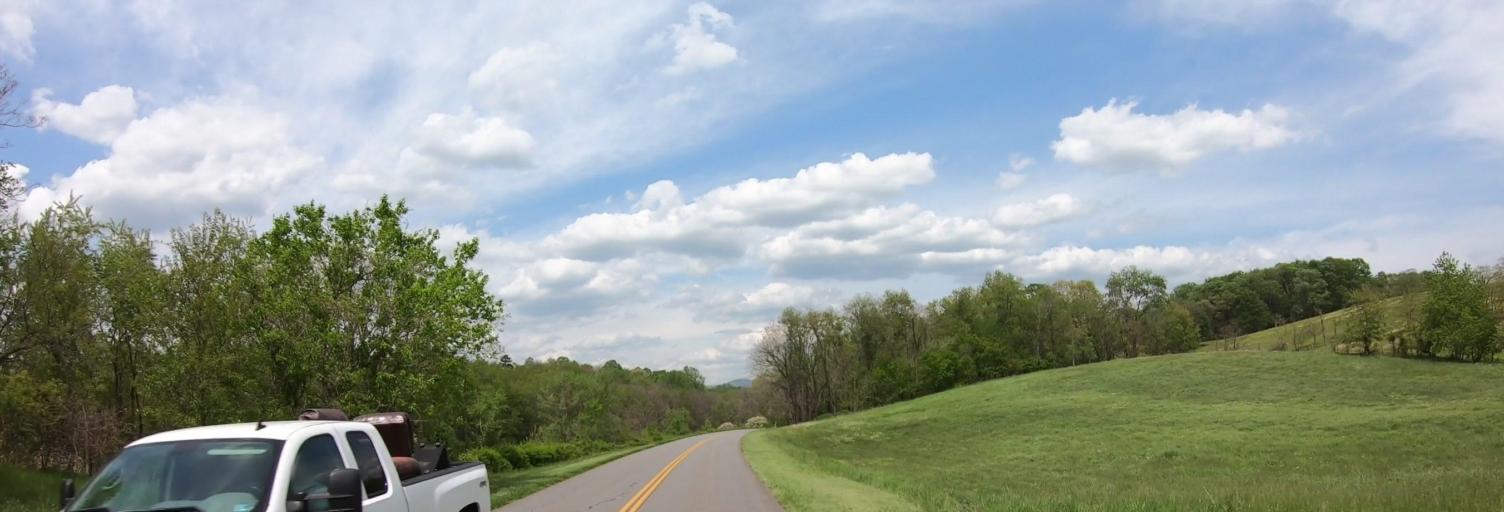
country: US
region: Virginia
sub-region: Botetourt County
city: Laymantown
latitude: 37.3284
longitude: -79.8567
